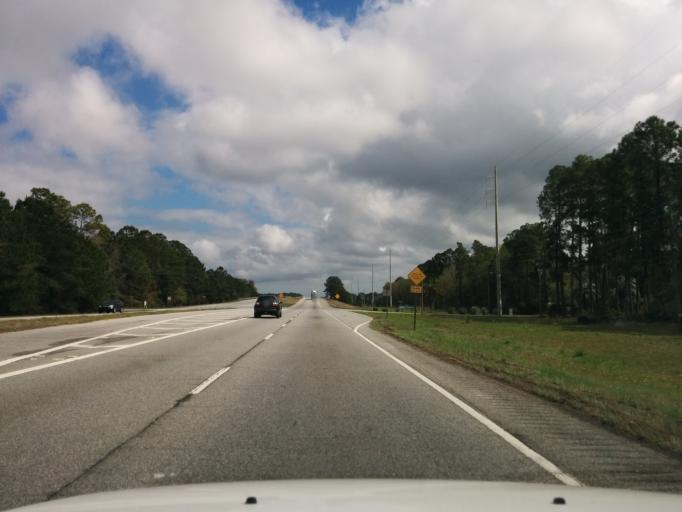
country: US
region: Georgia
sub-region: Glynn County
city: Brunswick
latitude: 31.1296
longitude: -81.5566
